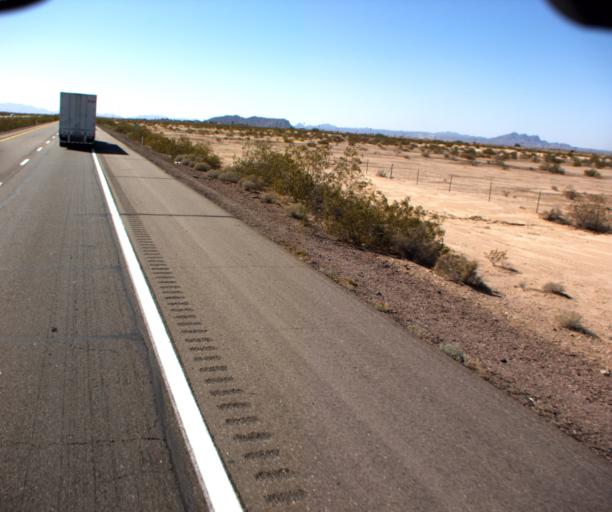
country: US
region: Arizona
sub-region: Yuma County
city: Wellton
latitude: 32.6989
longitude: -113.9195
